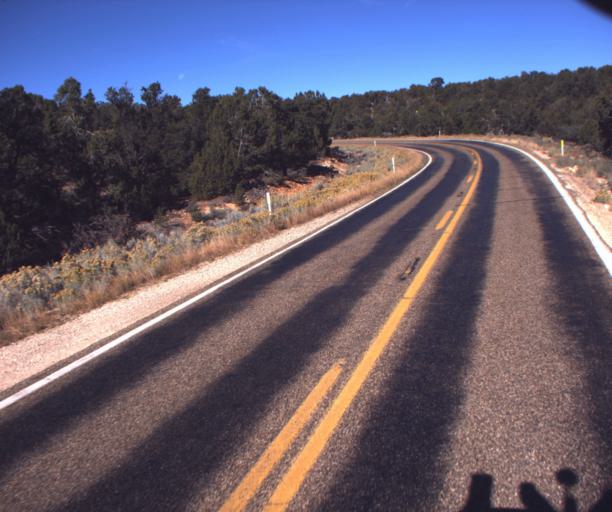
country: US
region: Arizona
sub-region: Coconino County
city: Fredonia
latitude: 36.7392
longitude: -112.1013
